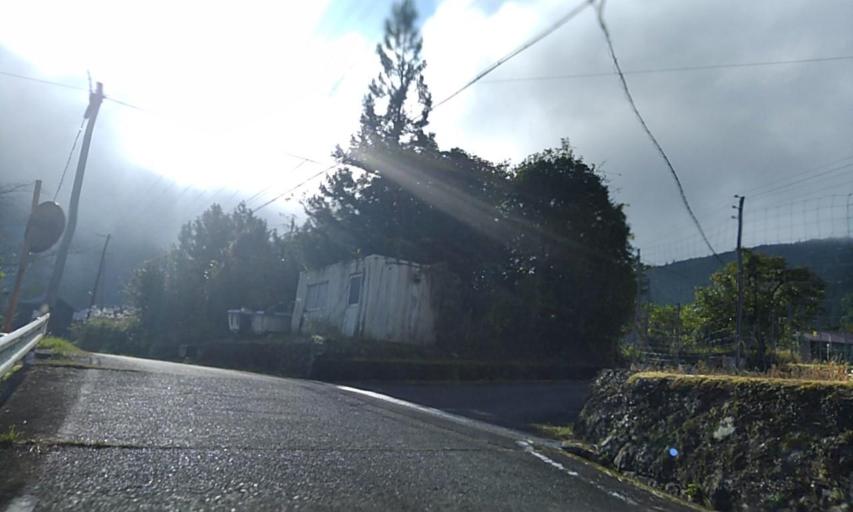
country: JP
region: Wakayama
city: Shingu
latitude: 33.9215
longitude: 135.9829
